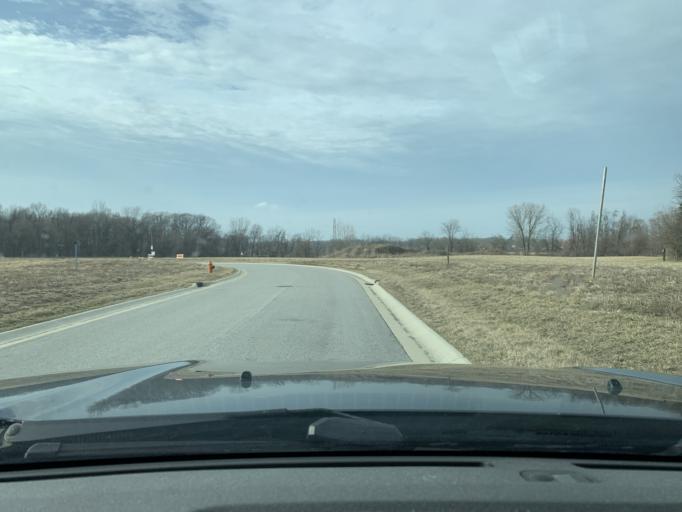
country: US
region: Indiana
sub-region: Porter County
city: Chesterton
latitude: 41.5556
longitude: -87.0529
